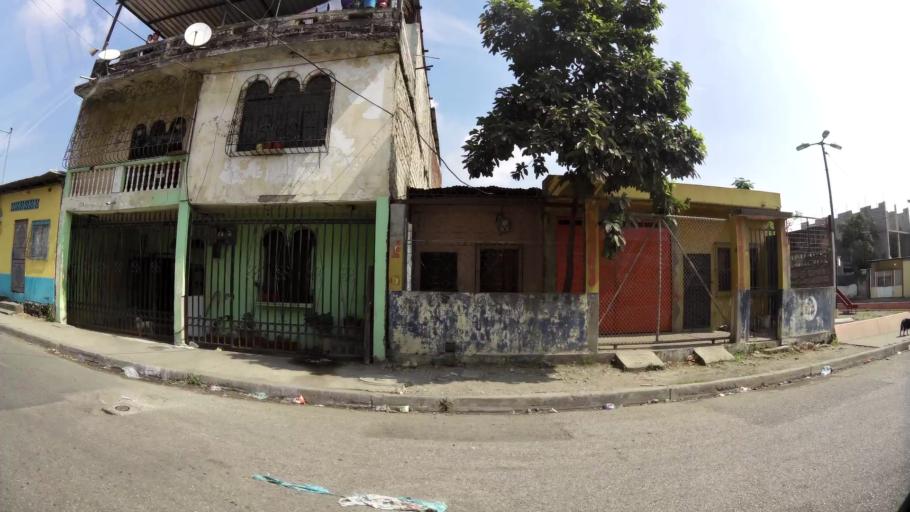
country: EC
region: Guayas
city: Guayaquil
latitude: -2.2631
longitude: -79.8882
